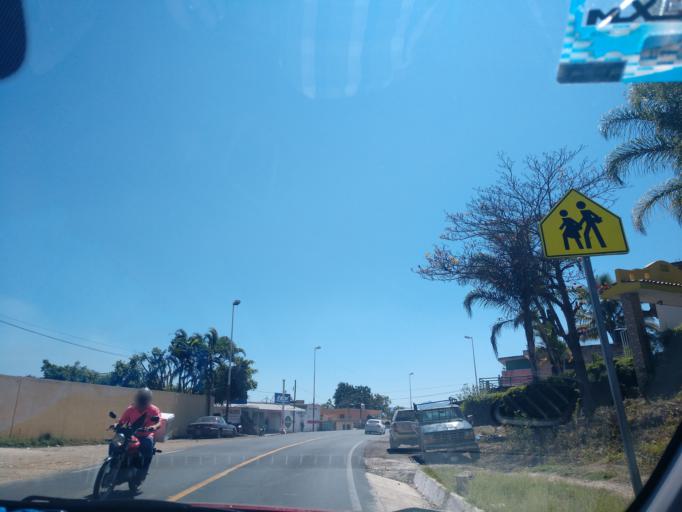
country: MX
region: Nayarit
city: Xalisco
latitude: 21.4025
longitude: -104.8953
